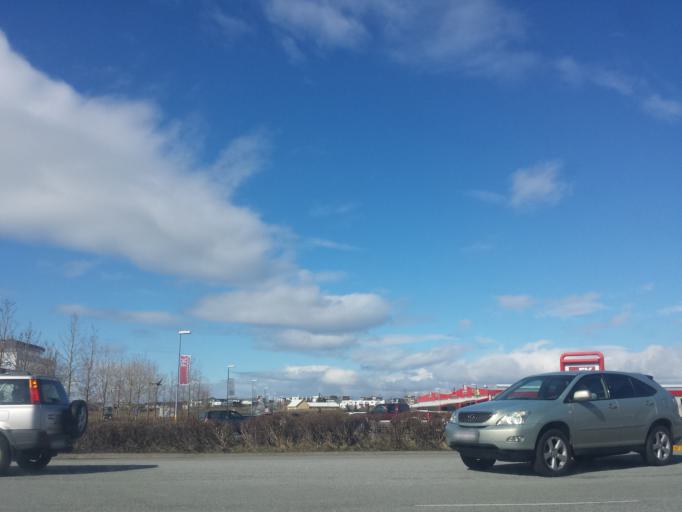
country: IS
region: Capital Region
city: Hafnarfjoerdur
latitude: 64.0812
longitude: -21.9411
